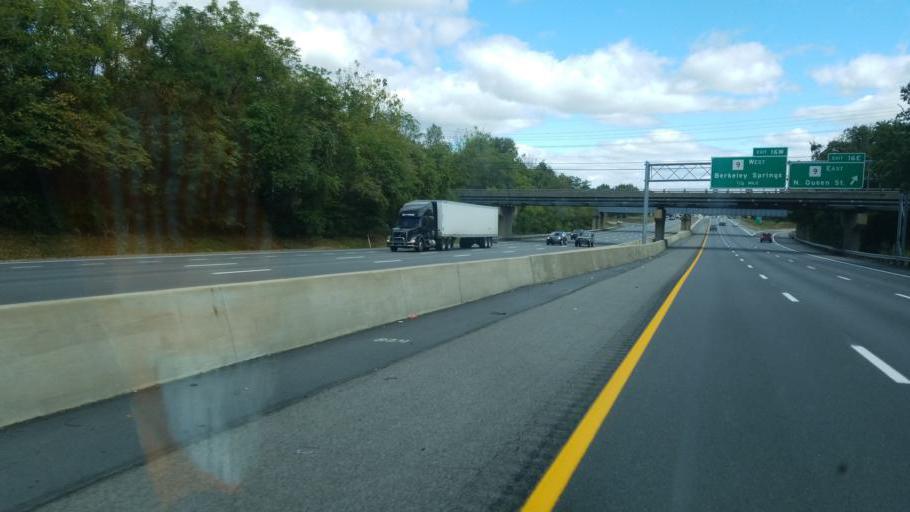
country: US
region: West Virginia
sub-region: Berkeley County
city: Martinsburg
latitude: 39.4936
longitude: -77.9660
